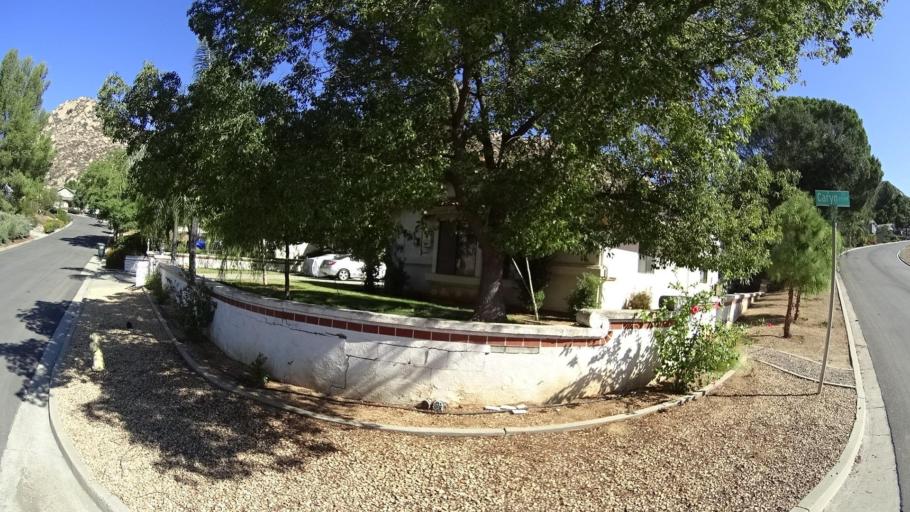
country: US
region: California
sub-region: San Diego County
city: San Diego Country Estates
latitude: 33.0038
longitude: -116.7685
